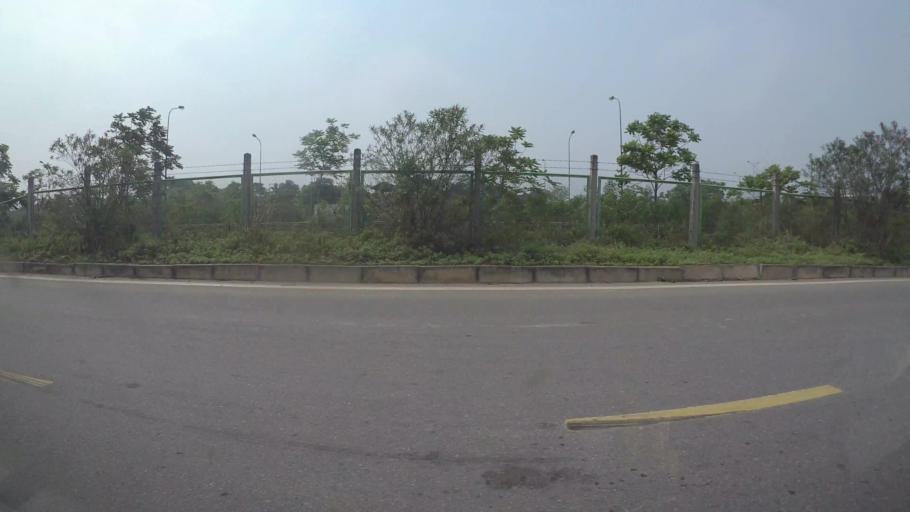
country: VN
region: Ha Noi
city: Lien Quan
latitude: 20.9909
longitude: 105.5371
